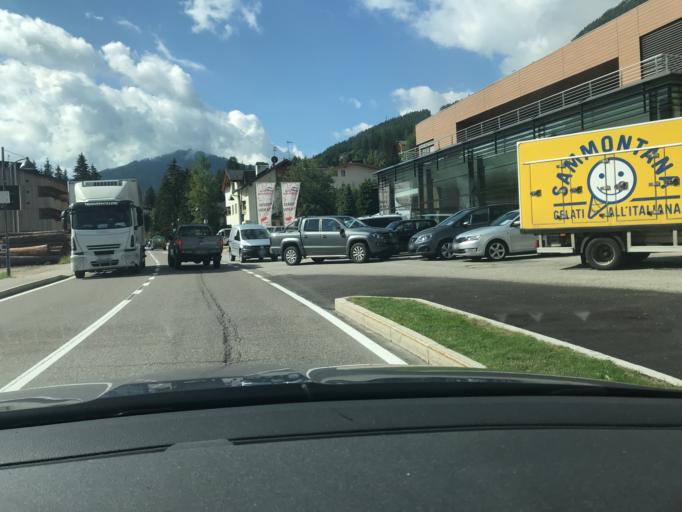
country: IT
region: Trentino-Alto Adige
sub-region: Bolzano
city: Badia
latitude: 46.6049
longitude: 11.8960
